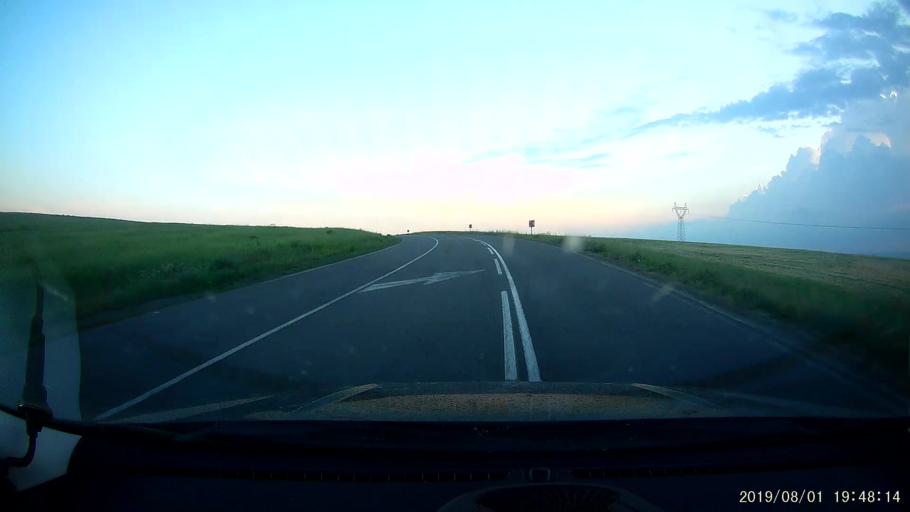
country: BG
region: Burgas
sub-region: Obshtina Karnobat
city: Karnobat
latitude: 42.6401
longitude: 26.9525
